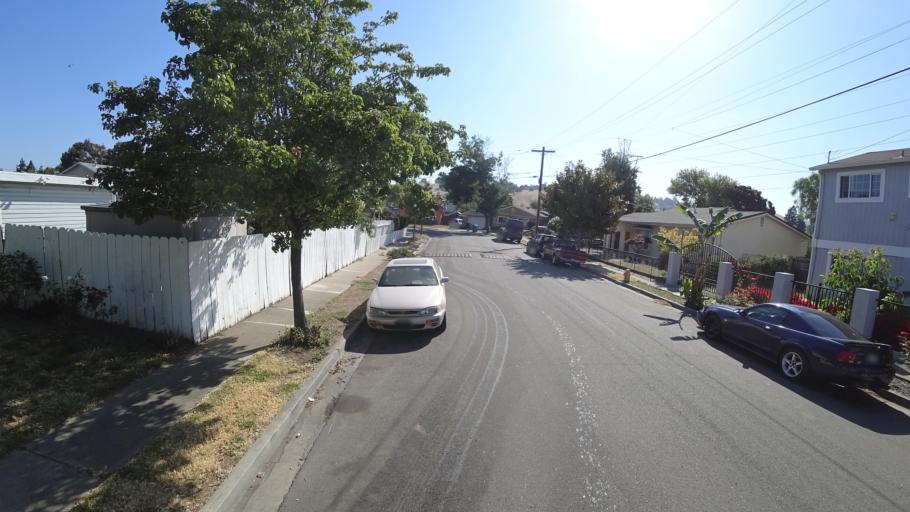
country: US
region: California
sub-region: Alameda County
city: Hayward
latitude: 37.6560
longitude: -122.0777
